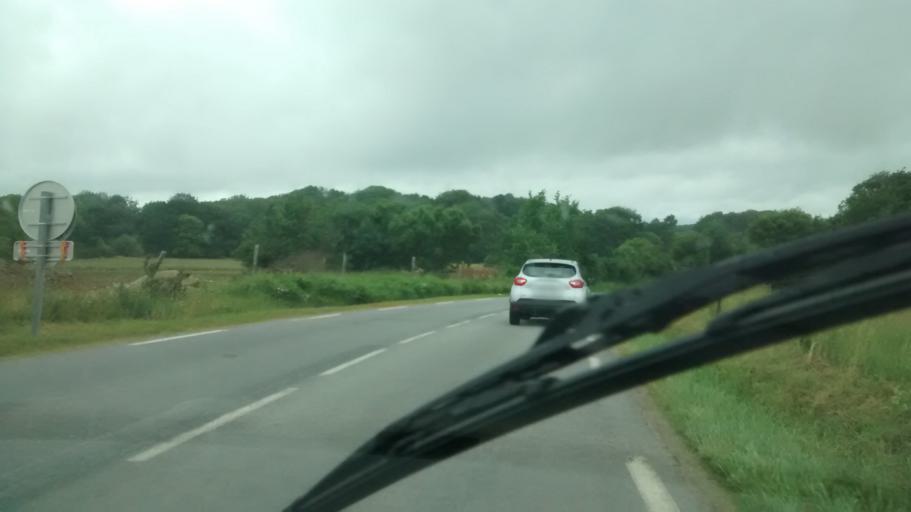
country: FR
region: Brittany
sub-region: Departement du Morbihan
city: Queven
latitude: 47.7643
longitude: -3.4252
